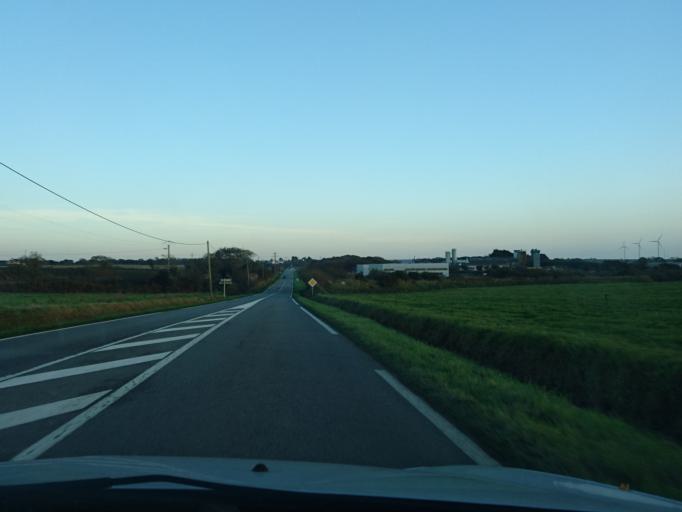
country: FR
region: Brittany
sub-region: Departement du Finistere
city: Lanrivoare
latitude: 48.4747
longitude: -4.6518
